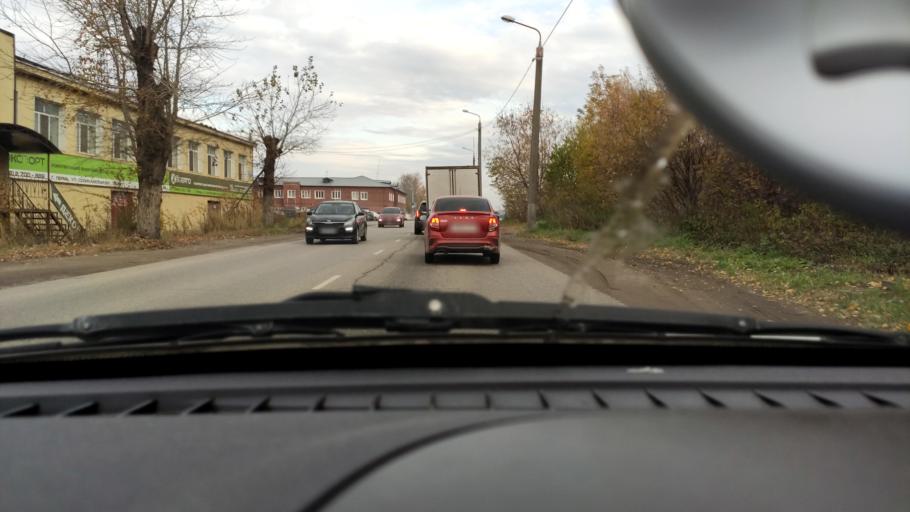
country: RU
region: Perm
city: Perm
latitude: 58.0924
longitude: 56.3544
